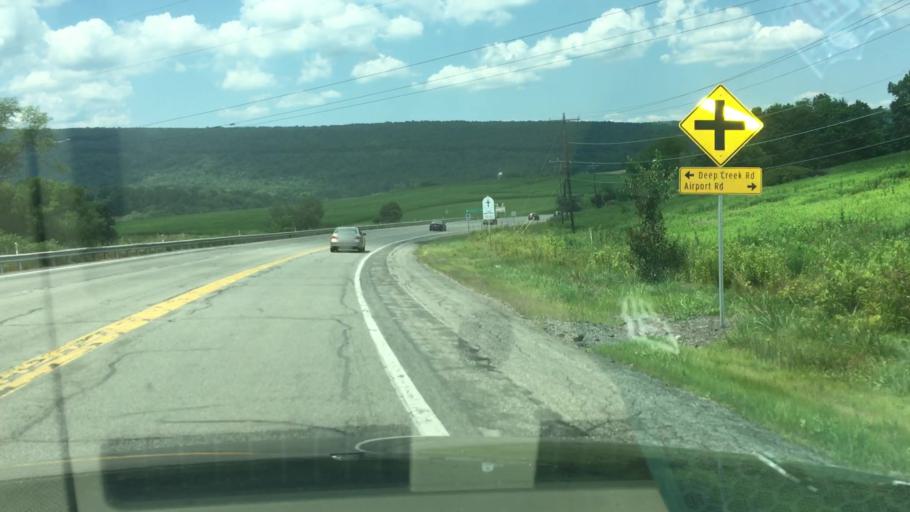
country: US
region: Pennsylvania
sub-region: Schuylkill County
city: Ashland
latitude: 40.7259
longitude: -76.3905
